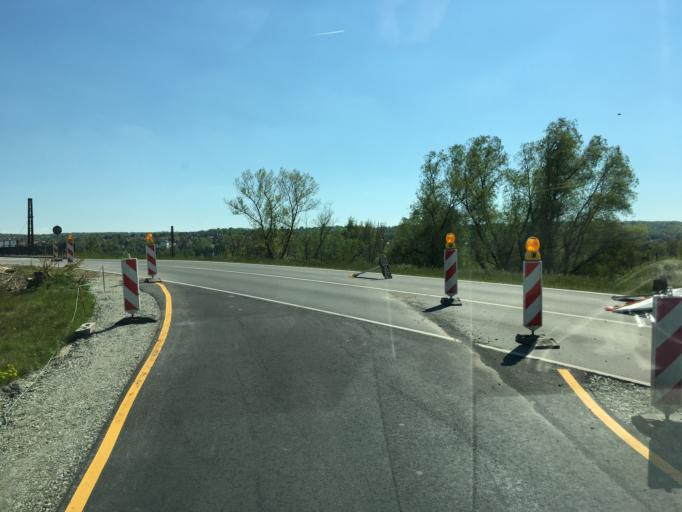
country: DE
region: Saxony-Anhalt
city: Naumburg
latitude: 51.1617
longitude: 11.7907
